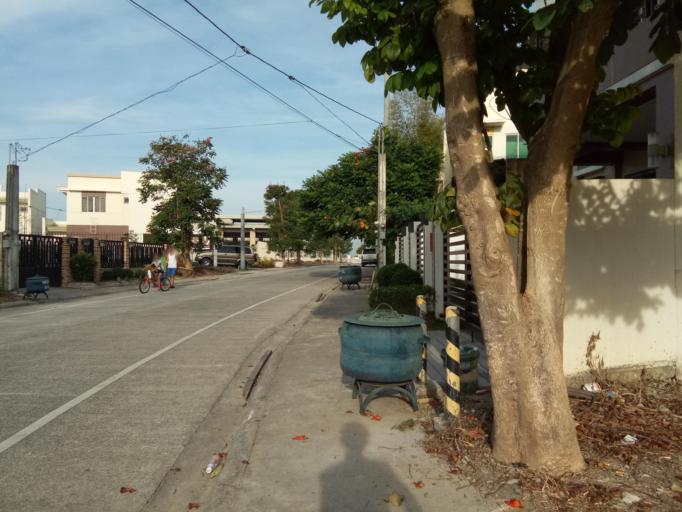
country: PH
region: Calabarzon
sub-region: Province of Cavite
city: Biga
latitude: 14.2775
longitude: 120.9718
